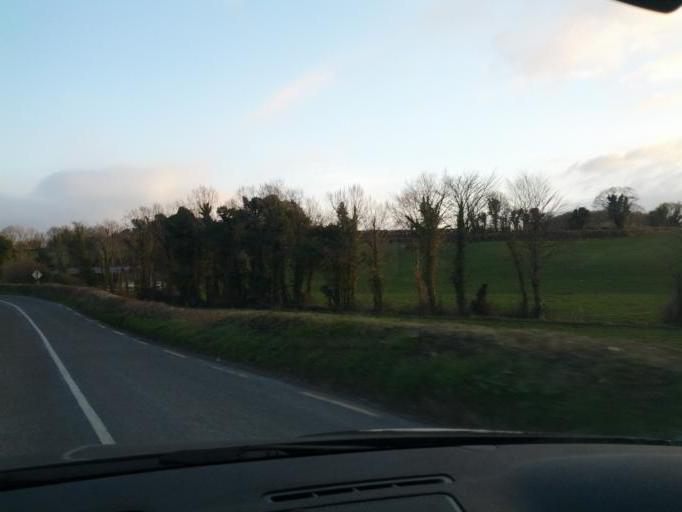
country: IE
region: Munster
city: Nenagh Bridge
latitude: 52.9559
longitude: -8.2337
